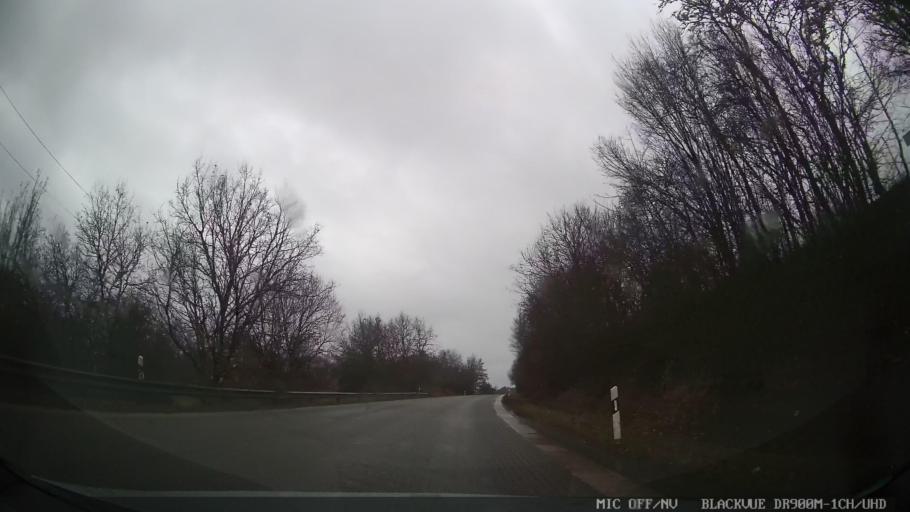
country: DE
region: Rheinland-Pfalz
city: Idar-Oberstein
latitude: 49.7118
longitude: 7.3033
